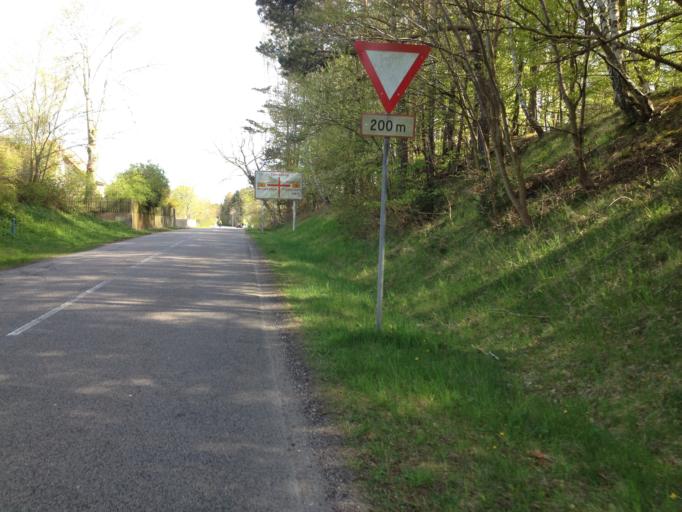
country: DK
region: Capital Region
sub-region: Halsnaes Kommune
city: Hundested
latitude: 55.9585
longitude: 11.9019
